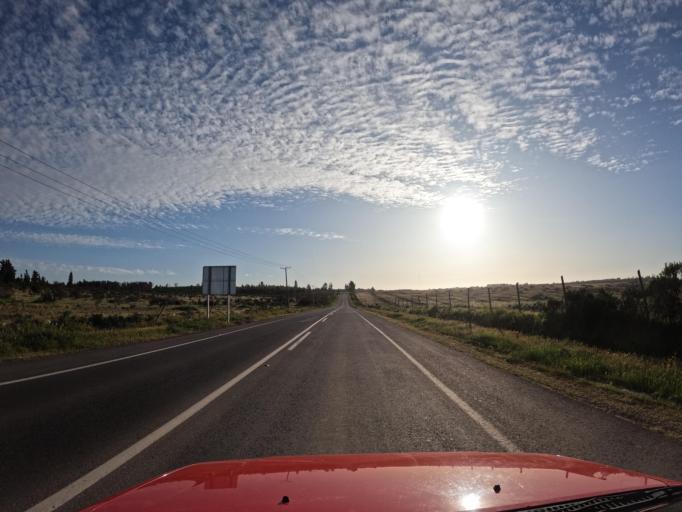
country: CL
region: Valparaiso
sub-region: San Antonio Province
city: San Antonio
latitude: -34.0738
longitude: -71.6356
